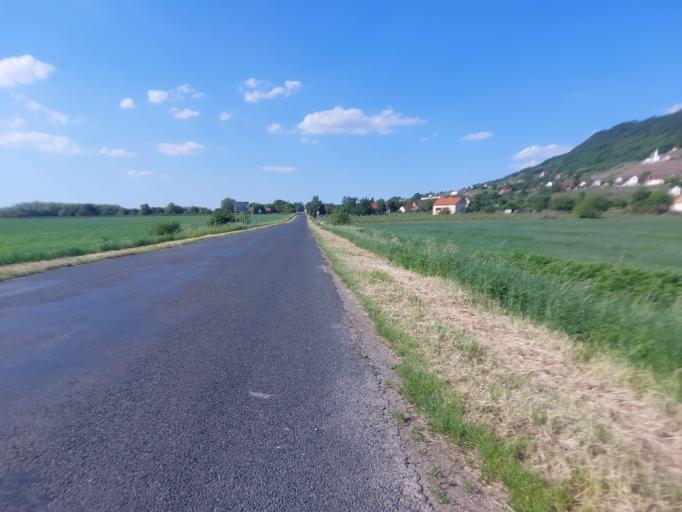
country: HU
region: Veszprem
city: Devecser
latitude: 47.1360
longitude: 17.3587
